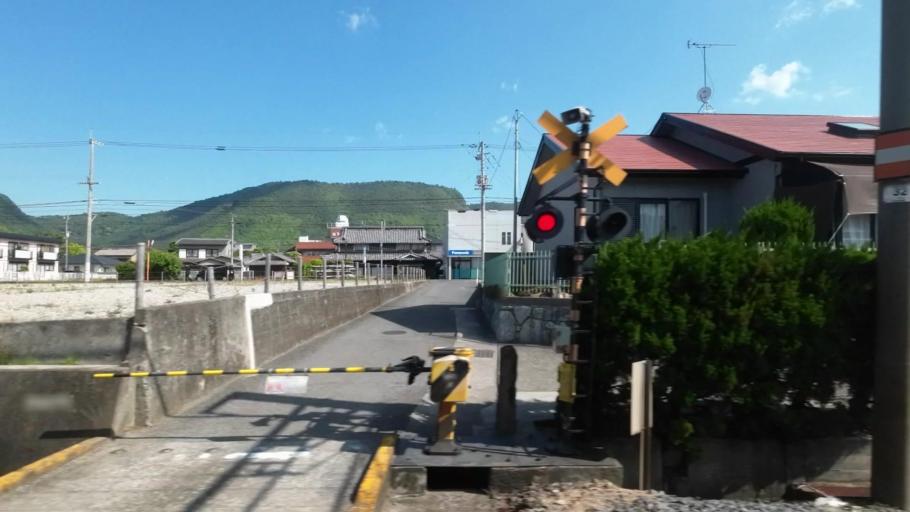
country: JP
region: Kagawa
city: Takamatsu-shi
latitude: 34.3010
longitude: 133.9470
